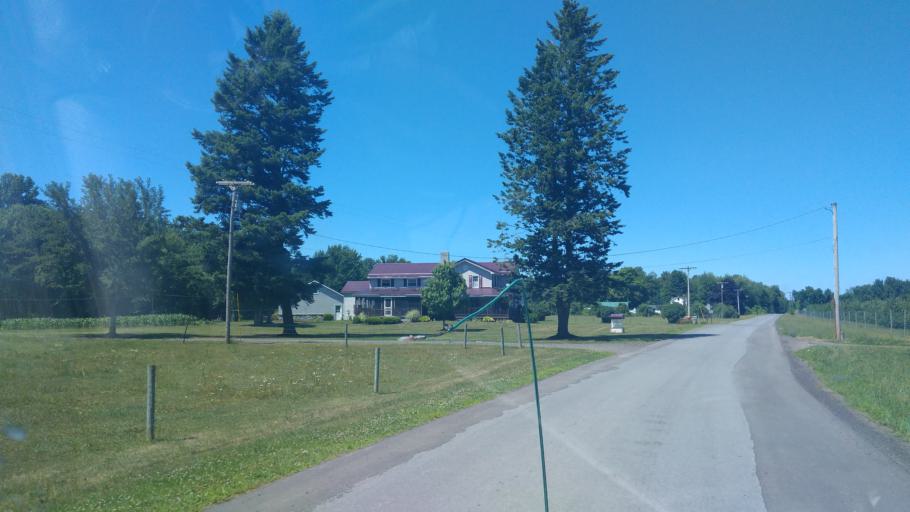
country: US
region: New York
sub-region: Wayne County
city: Sodus
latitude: 43.1854
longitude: -76.9801
